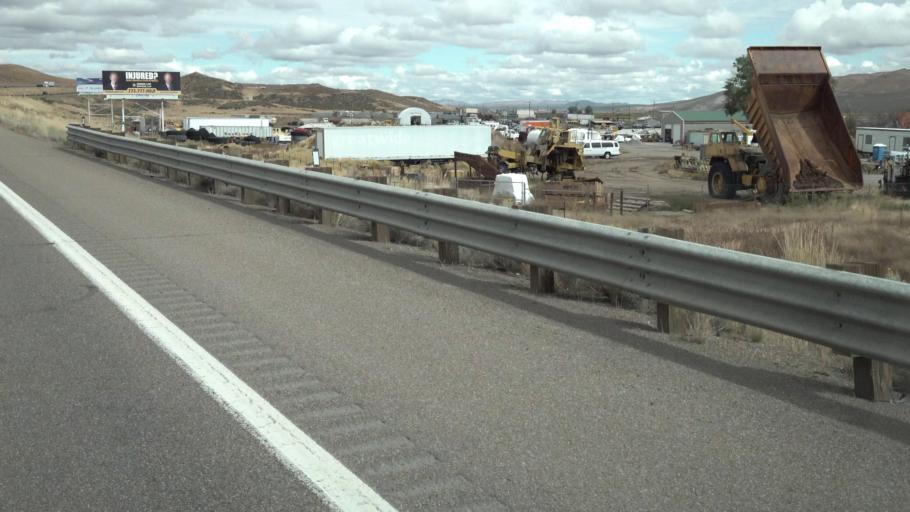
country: US
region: Nevada
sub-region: Elko County
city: Elko
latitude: 40.8883
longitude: -115.7134
